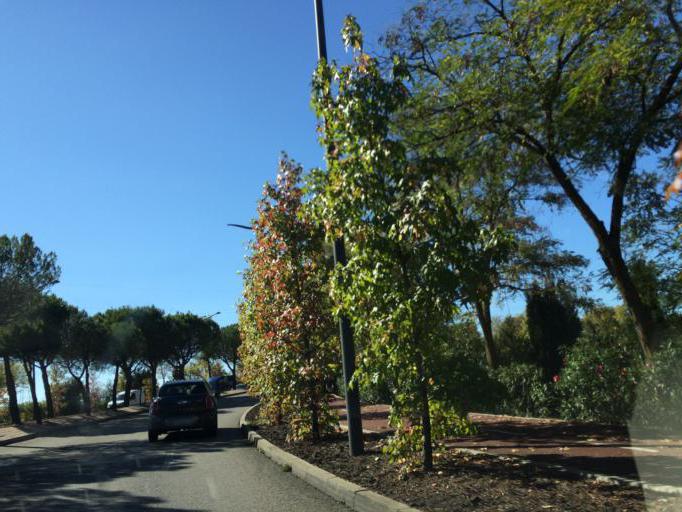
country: ES
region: Madrid
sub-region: Provincia de Madrid
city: Tres Cantos
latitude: 40.5866
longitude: -3.7038
